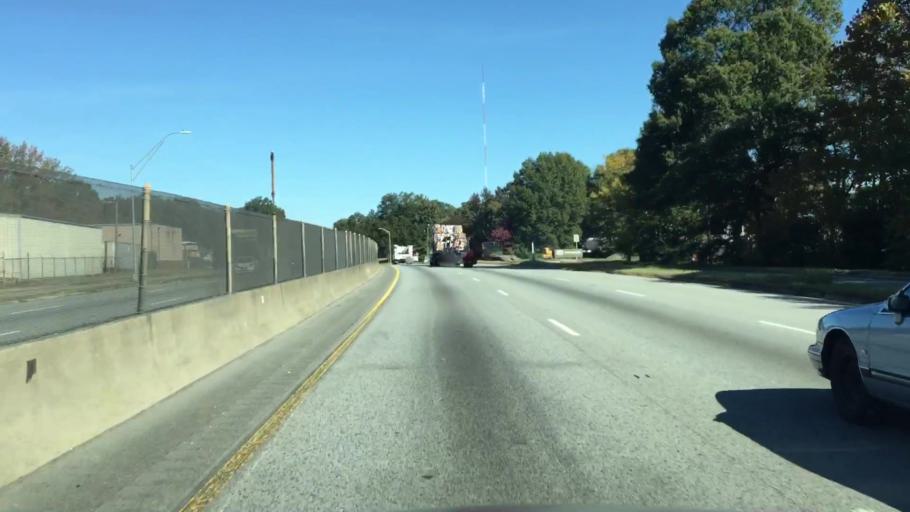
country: US
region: North Carolina
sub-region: Guilford County
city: Greensboro
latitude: 36.0903
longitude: -79.7659
